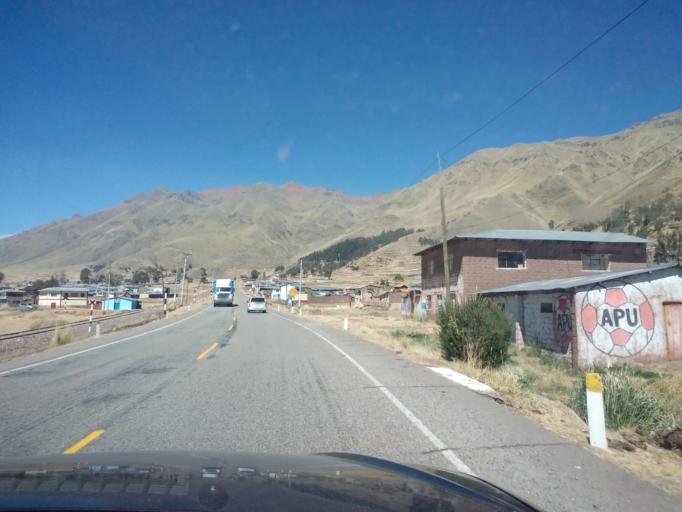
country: PE
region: Cusco
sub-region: Provincia de Canchis
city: Marangani
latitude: -14.4136
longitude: -71.1177
